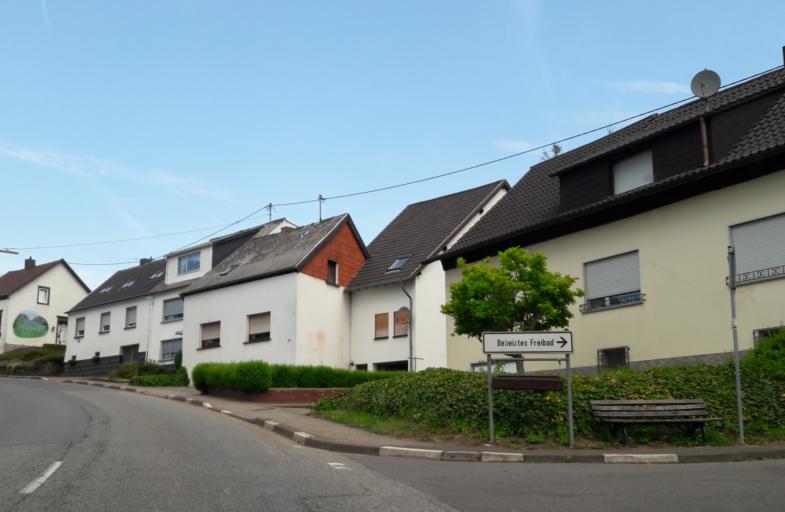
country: DE
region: Saarland
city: Illingen
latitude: 49.3839
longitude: 7.0175
